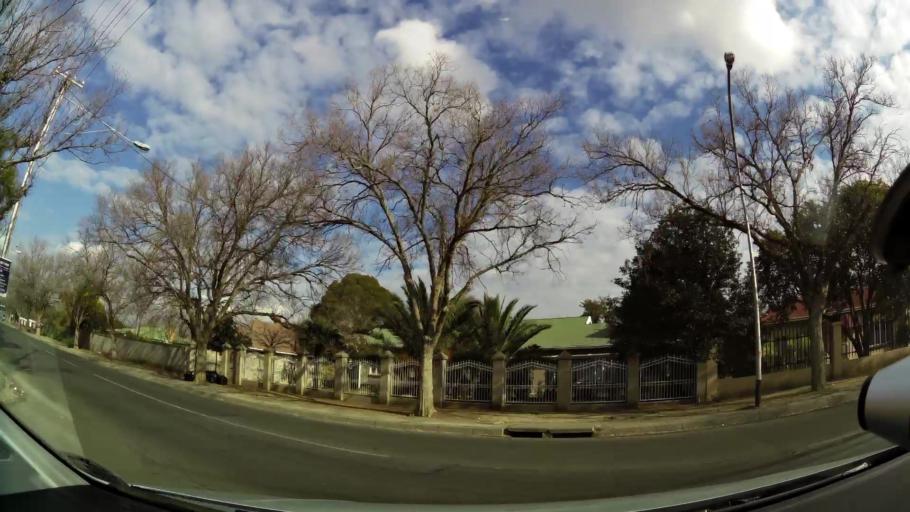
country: ZA
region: Orange Free State
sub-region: Mangaung Metropolitan Municipality
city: Bloemfontein
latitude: -29.0802
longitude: 26.2126
